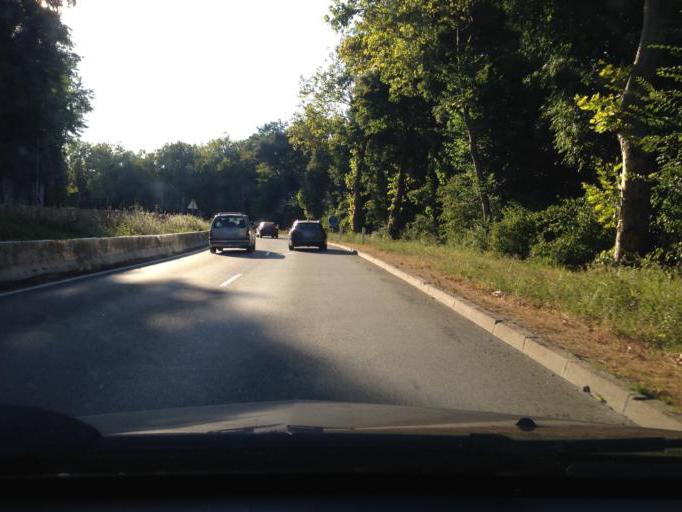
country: FR
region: Ile-de-France
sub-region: Departement des Yvelines
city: Louveciennes
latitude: 48.8727
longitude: 2.1096
